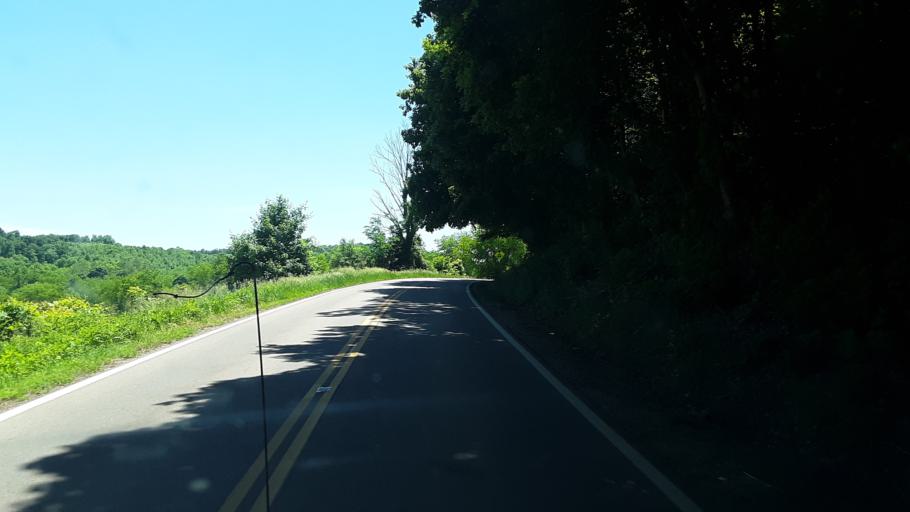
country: US
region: Ohio
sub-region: Coshocton County
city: Coshocton
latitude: 40.3170
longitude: -82.0157
